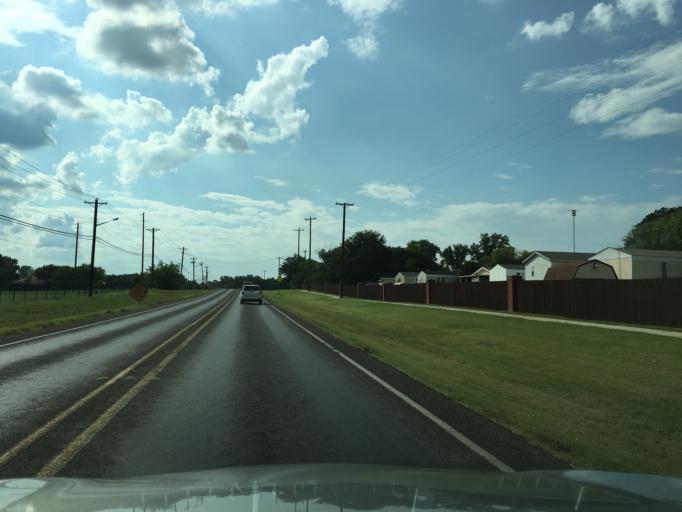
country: US
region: Texas
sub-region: Denton County
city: Corinth
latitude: 33.2067
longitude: -97.0729
